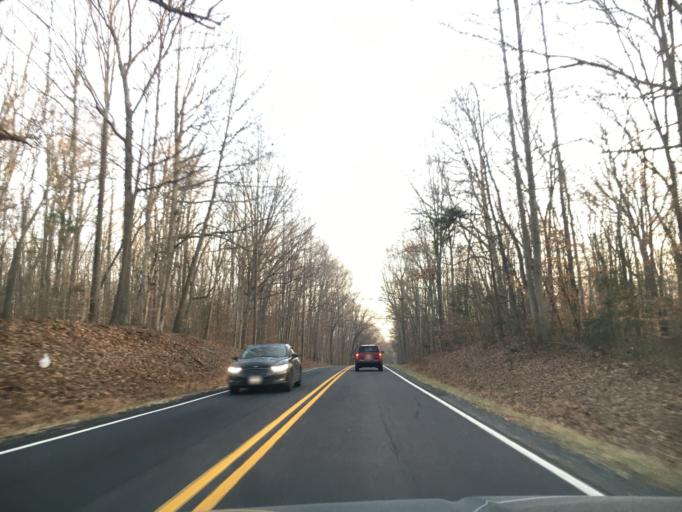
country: US
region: Virginia
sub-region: Louisa County
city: Louisa
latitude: 38.1554
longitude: -77.9284
